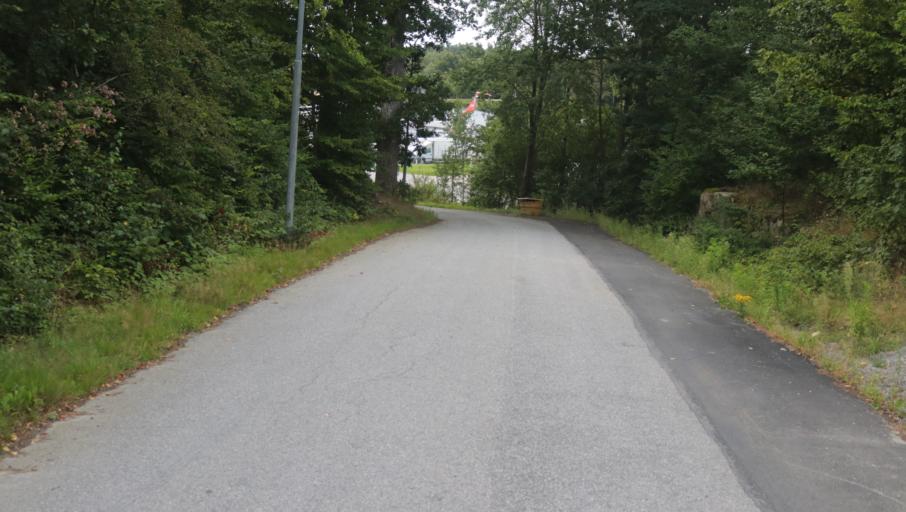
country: SE
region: Blekinge
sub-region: Karlshamns Kommun
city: Karlshamn
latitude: 56.1816
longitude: 14.8447
